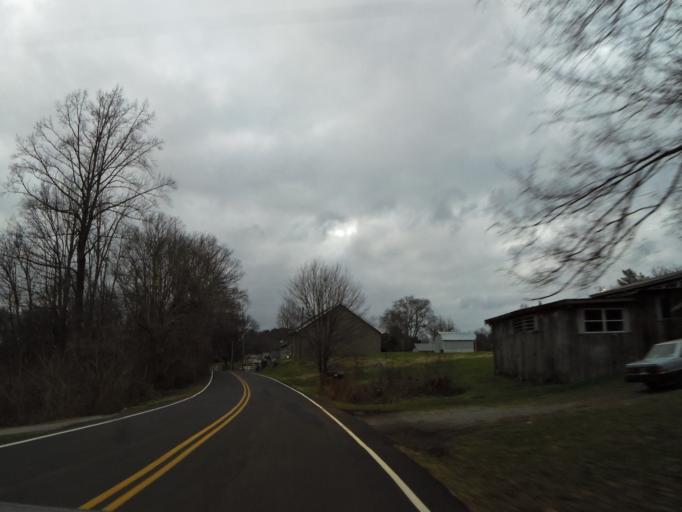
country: US
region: Tennessee
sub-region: Blount County
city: Eagleton Village
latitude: 35.8298
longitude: -83.9424
